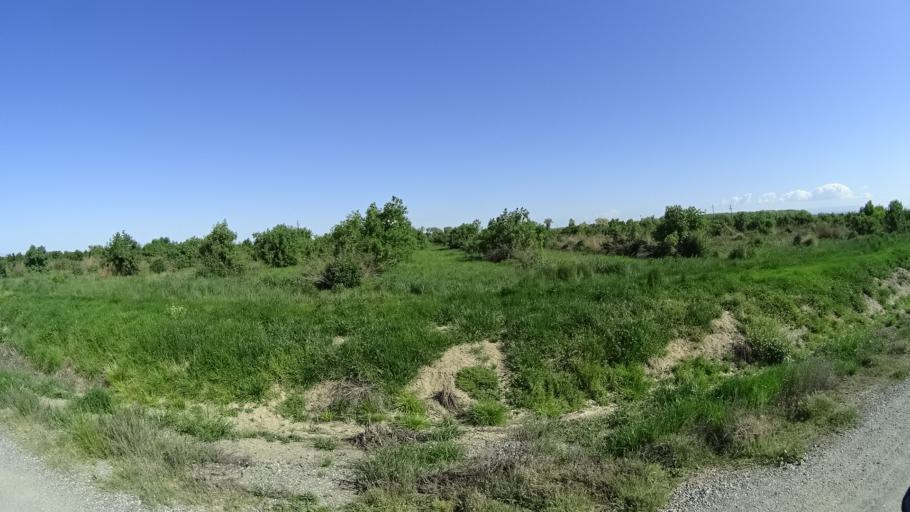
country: US
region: California
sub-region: Glenn County
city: Hamilton City
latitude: 39.7127
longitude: -121.9666
